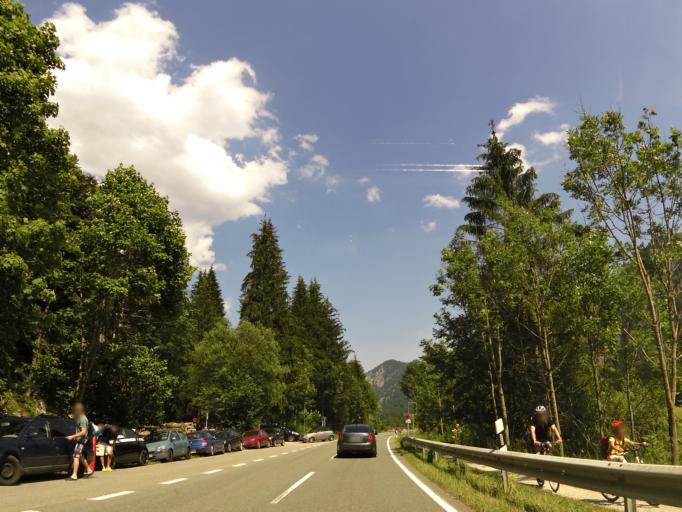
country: DE
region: Bavaria
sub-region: Upper Bavaria
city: Reit im Winkl
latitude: 47.6884
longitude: 12.5733
